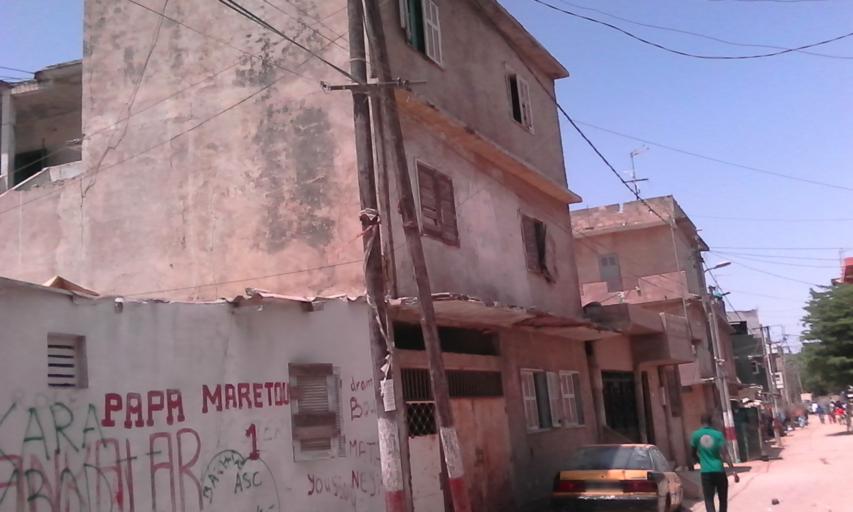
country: SN
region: Dakar
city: Grand Dakar
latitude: 14.7079
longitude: -17.4567
